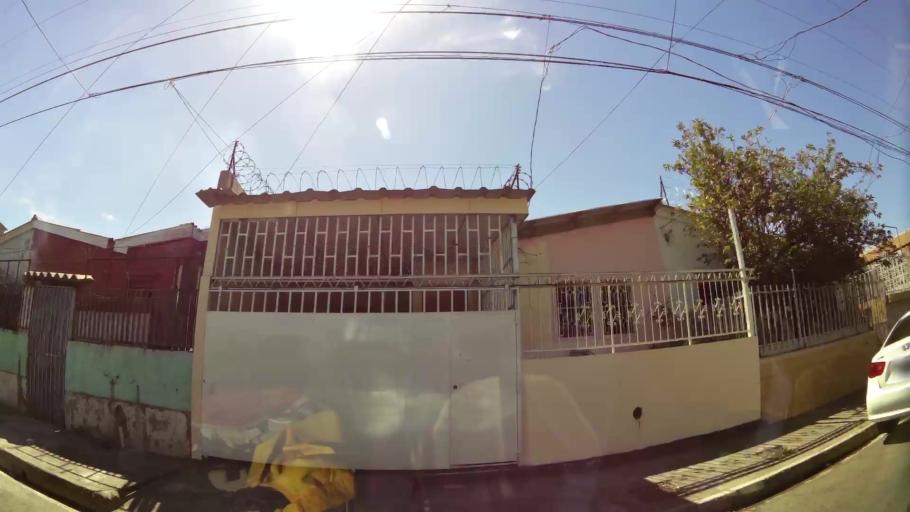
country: SV
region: San Miguel
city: San Miguel
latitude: 13.4787
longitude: -88.1680
